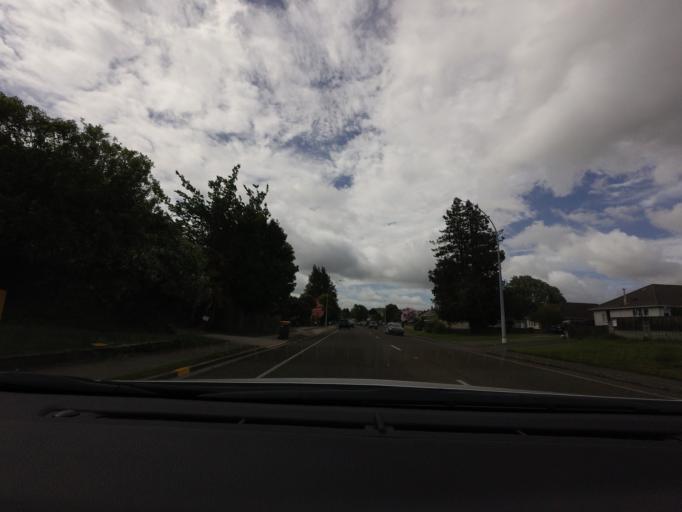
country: NZ
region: Bay of Plenty
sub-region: Rotorua District
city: Rotorua
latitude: -38.1514
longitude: 176.2398
